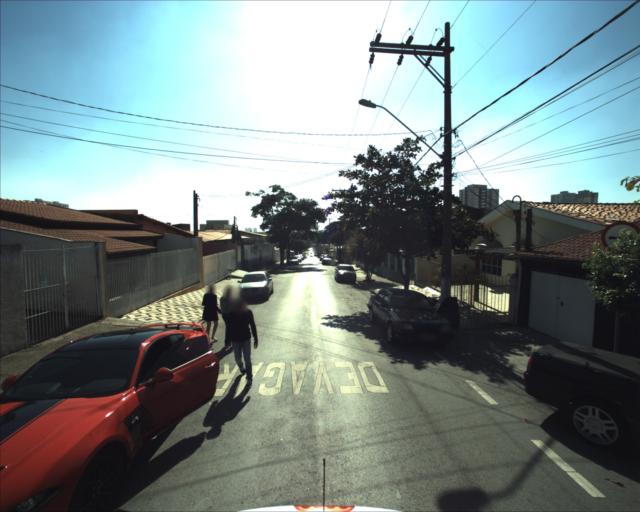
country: BR
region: Sao Paulo
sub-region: Sorocaba
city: Sorocaba
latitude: -23.4957
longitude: -47.4315
